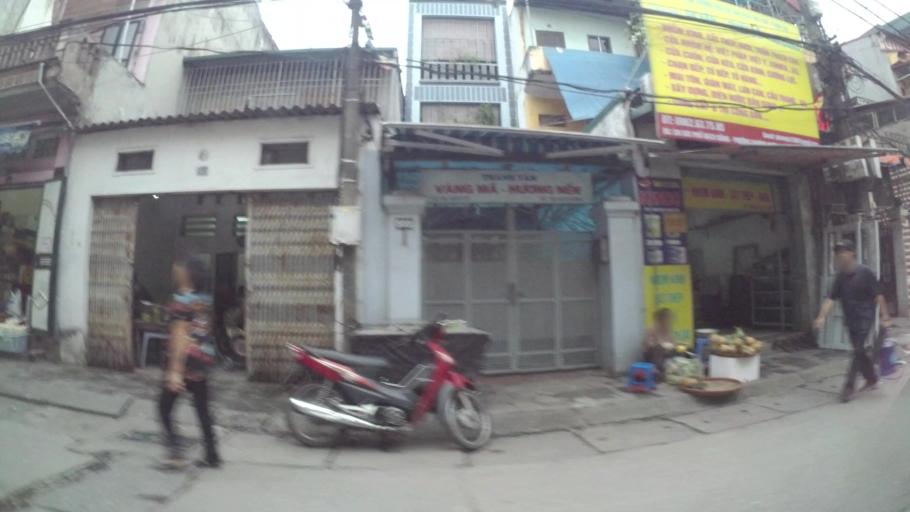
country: VN
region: Ha Noi
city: Hoan Kiem
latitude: 21.0240
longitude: 105.8623
